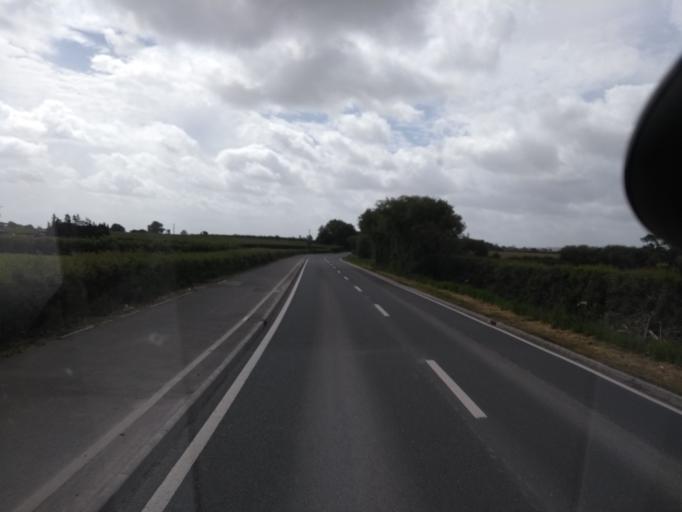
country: GB
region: England
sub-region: Somerset
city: Bridgwater
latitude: 51.1681
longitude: -3.0662
